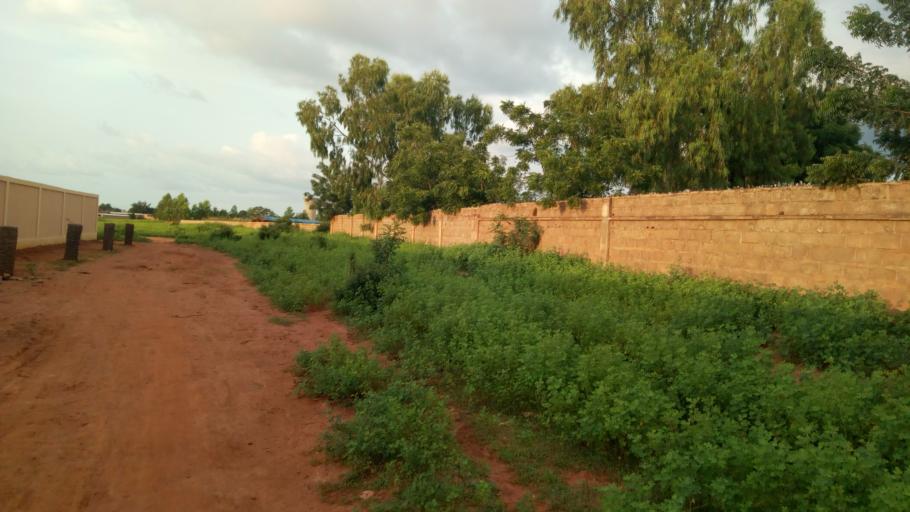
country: ML
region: Sikasso
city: Koutiala
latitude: 12.3737
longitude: -5.4766
